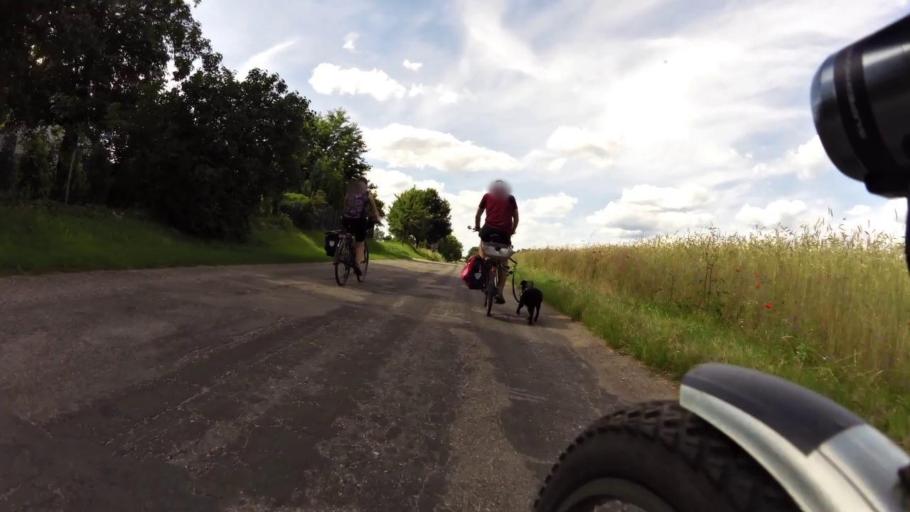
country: PL
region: West Pomeranian Voivodeship
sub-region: Powiat lobeski
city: Dobra
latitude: 53.5867
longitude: 15.3895
